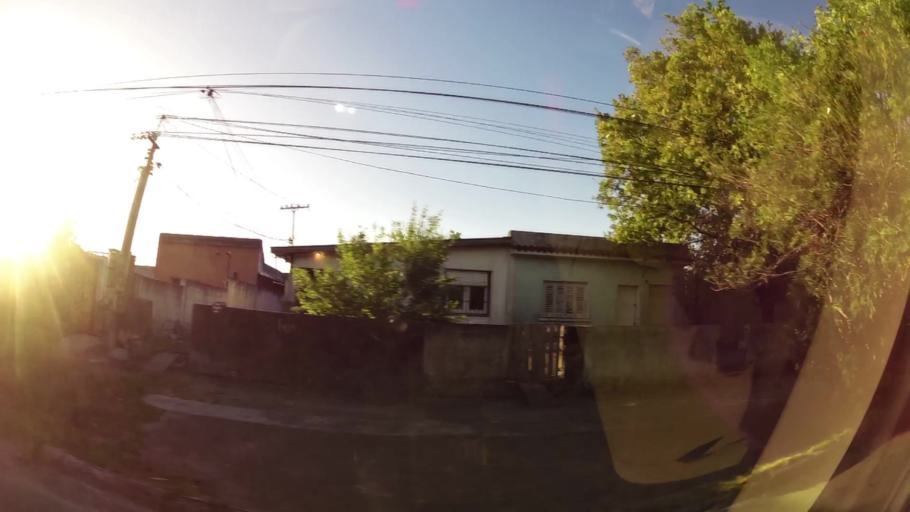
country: UY
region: Montevideo
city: Montevideo
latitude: -34.8368
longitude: -56.1967
